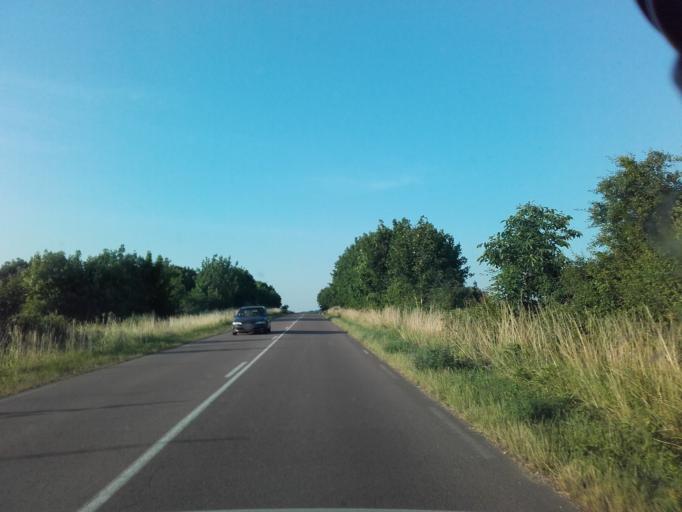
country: FR
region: Bourgogne
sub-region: Departement de Saone-et-Loire
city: Rully
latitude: 46.8744
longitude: 4.7523
